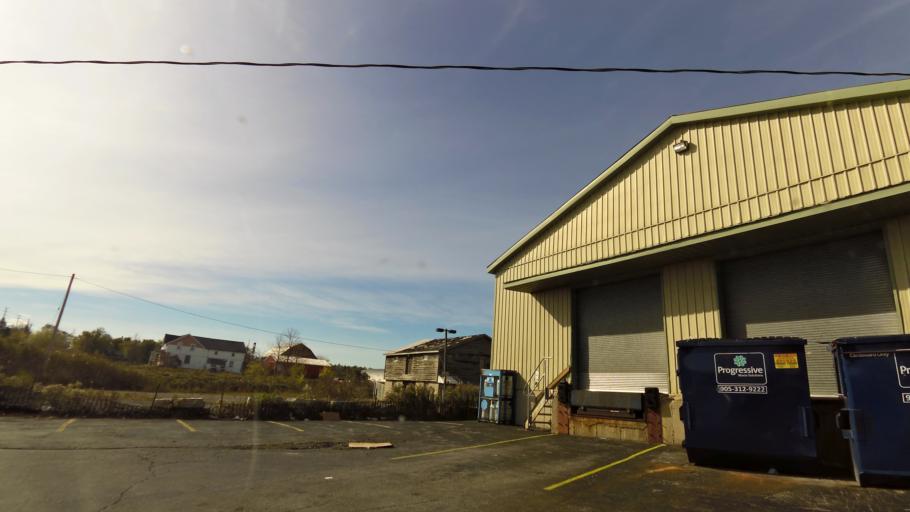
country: CA
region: Ontario
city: Oakville
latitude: 43.5013
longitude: -79.7389
